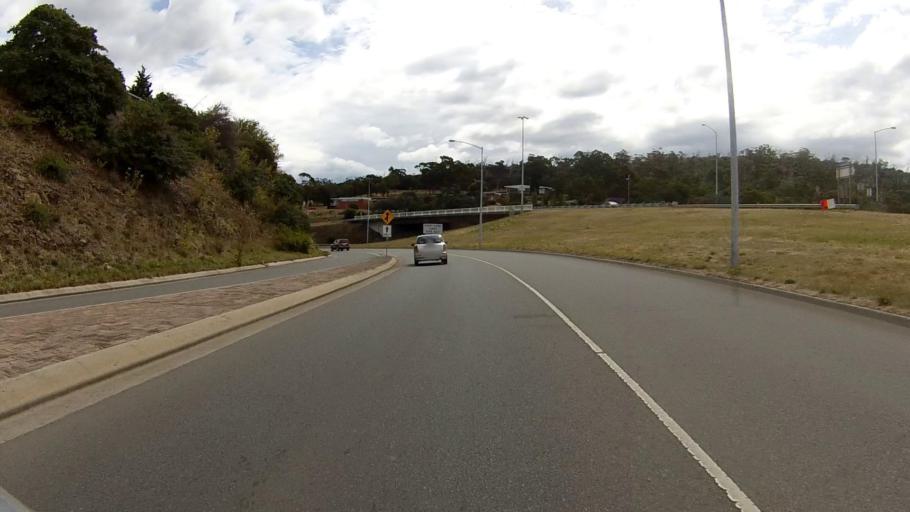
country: AU
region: Tasmania
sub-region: Clarence
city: Bellerive
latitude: -42.8633
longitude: 147.3640
